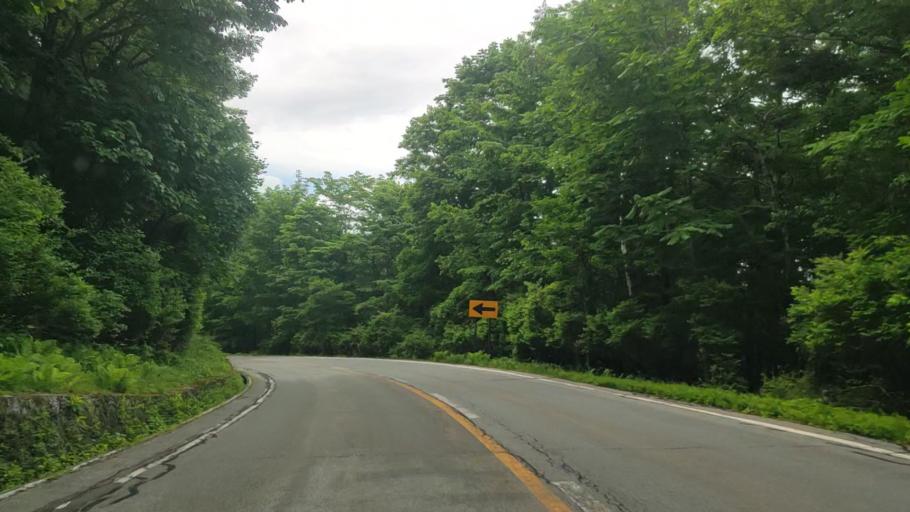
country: JP
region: Yamanashi
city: Fujikawaguchiko
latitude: 35.4202
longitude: 138.7398
